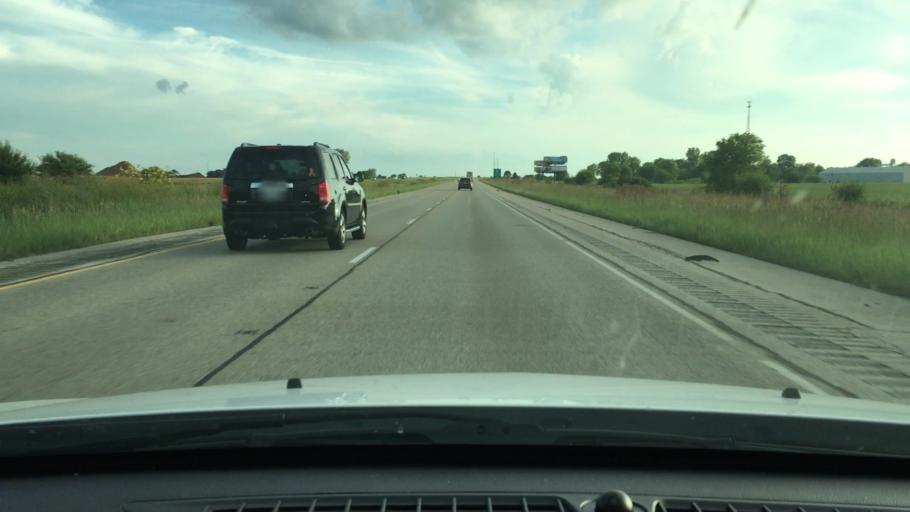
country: US
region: Illinois
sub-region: Logan County
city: Atlanta
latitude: 40.3208
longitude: -89.1576
